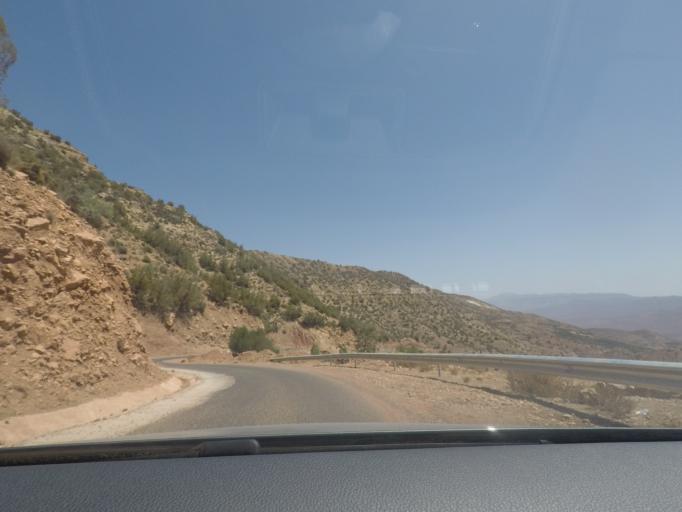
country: MA
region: Souss-Massa-Draa
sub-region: Taroudannt
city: Bigoudine
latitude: 30.7457
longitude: -9.2813
